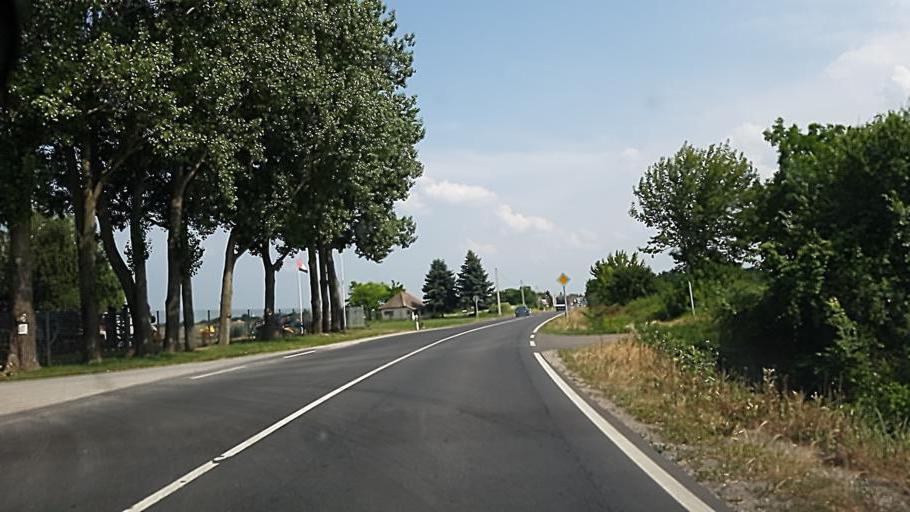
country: HU
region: Heves
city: Poroszlo
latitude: 47.6466
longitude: 20.6318
